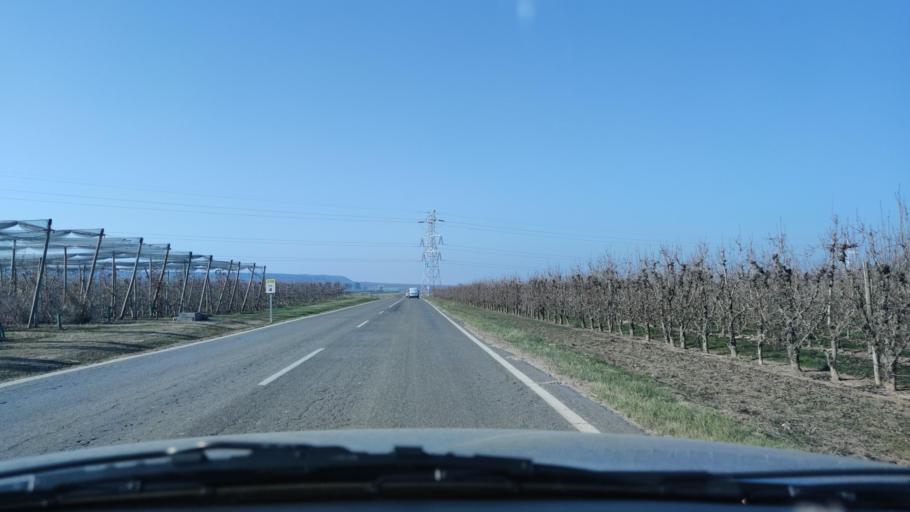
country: ES
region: Catalonia
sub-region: Provincia de Lleida
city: Juneda
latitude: 41.5714
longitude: 0.7597
